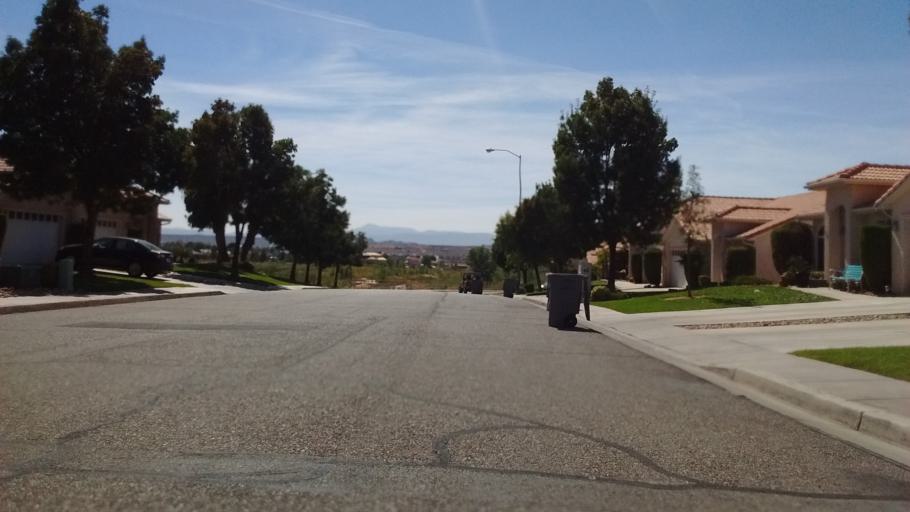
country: US
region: Utah
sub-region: Washington County
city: Washington
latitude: 37.1053
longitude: -113.5276
